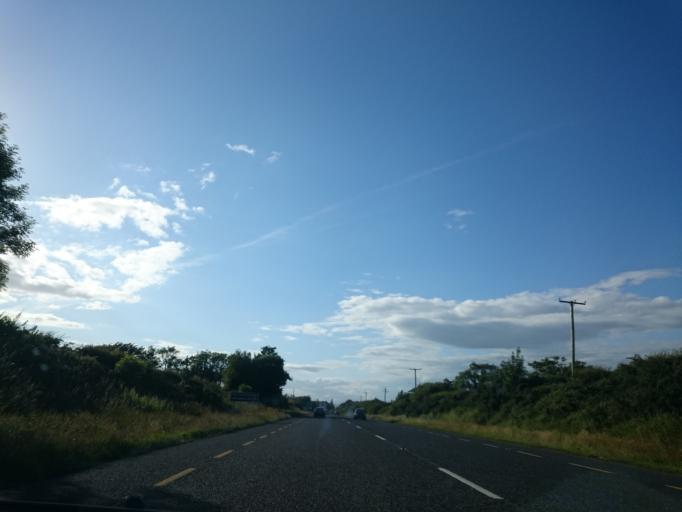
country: IE
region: Leinster
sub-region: Loch Garman
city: Loch Garman
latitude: 52.3186
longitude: -6.4965
